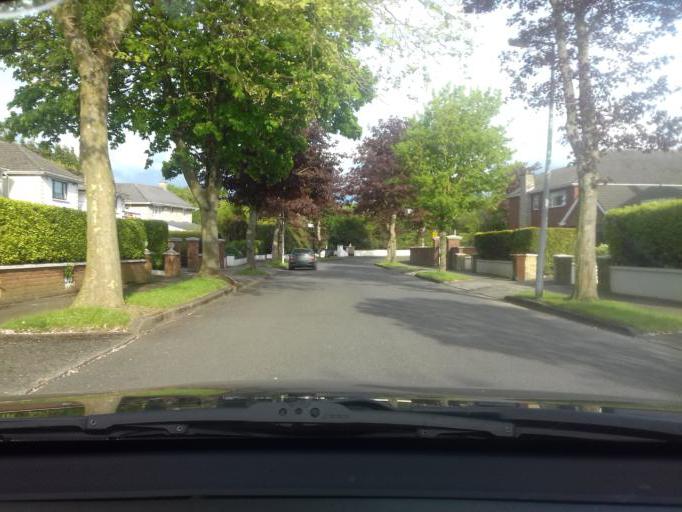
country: IE
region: Leinster
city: Castleknock
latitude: 53.3743
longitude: -6.3525
